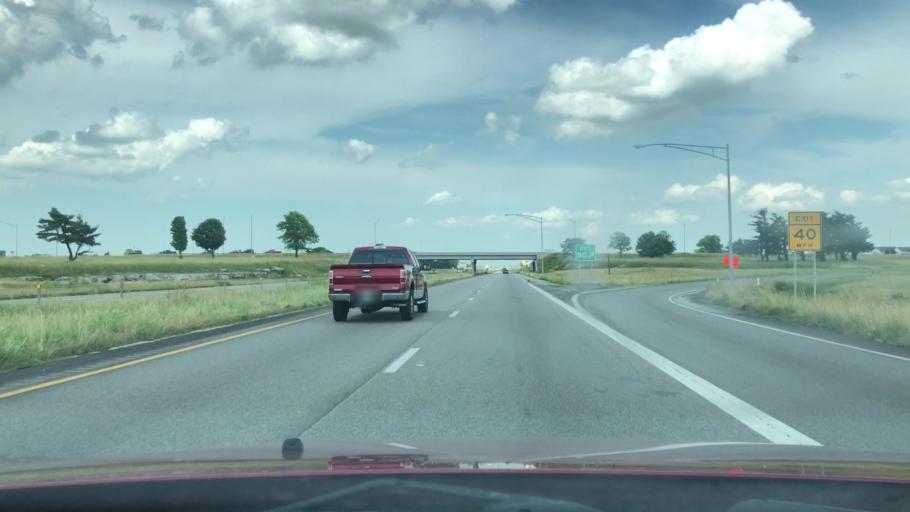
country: US
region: Missouri
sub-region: Greene County
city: Springfield
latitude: 37.2501
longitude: -93.2660
